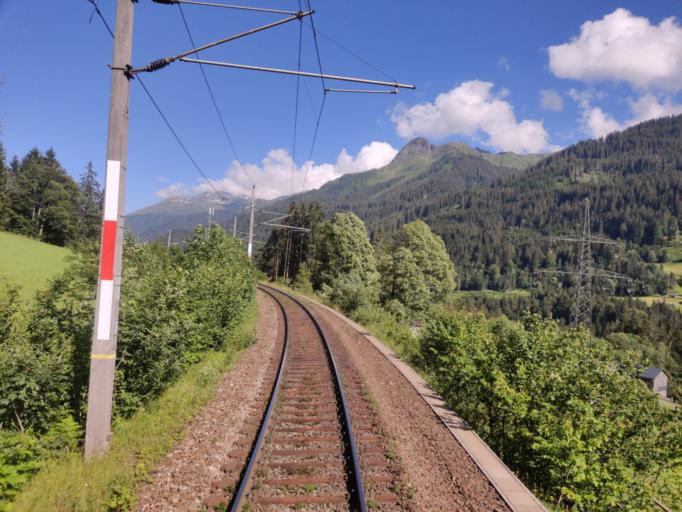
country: AT
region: Vorarlberg
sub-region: Politischer Bezirk Bludenz
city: Klosterle
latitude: 47.1317
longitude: 10.0409
